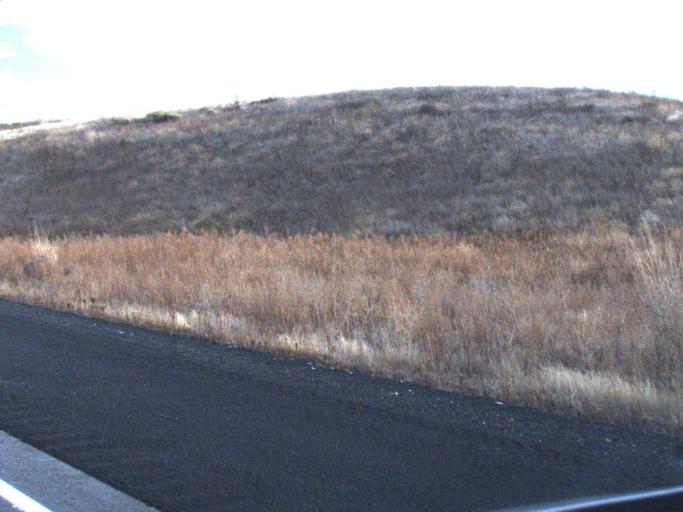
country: US
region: Washington
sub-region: Franklin County
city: Connell
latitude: 46.8687
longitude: -118.6309
